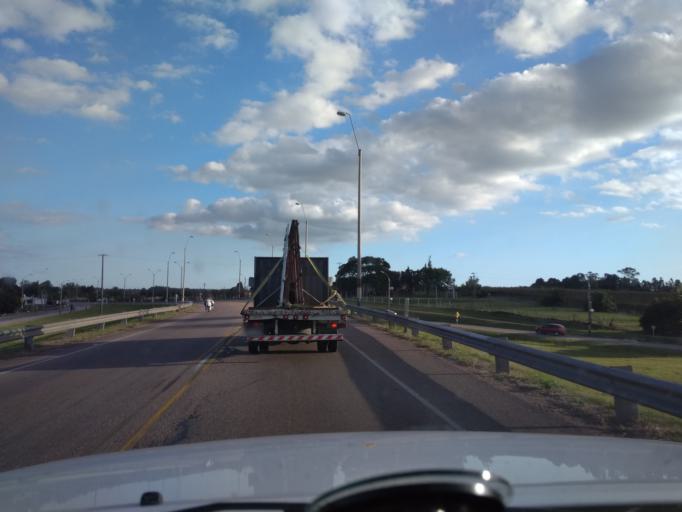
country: UY
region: Canelones
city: Canelones
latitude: -34.5435
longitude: -56.2745
